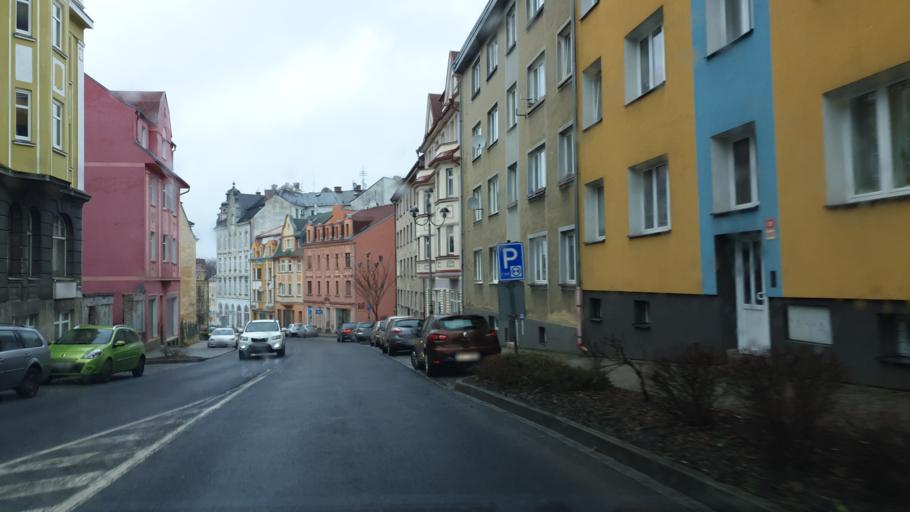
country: CZ
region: Karlovarsky
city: As
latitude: 50.2170
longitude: 12.1953
